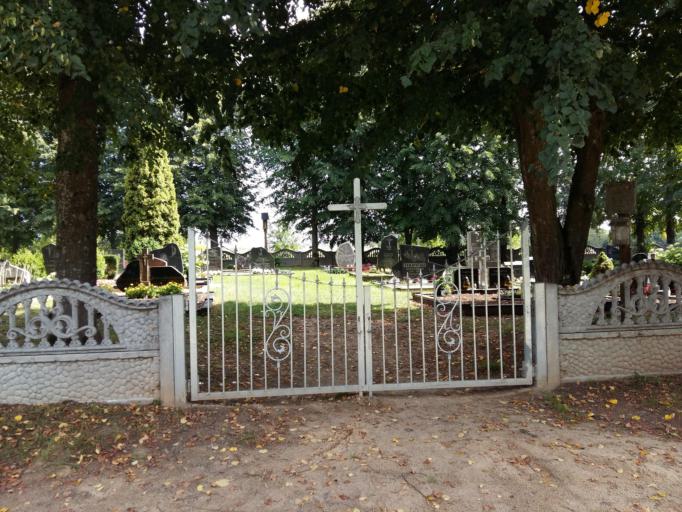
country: LT
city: Kaisiadorys
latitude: 54.8476
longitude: 24.3179
